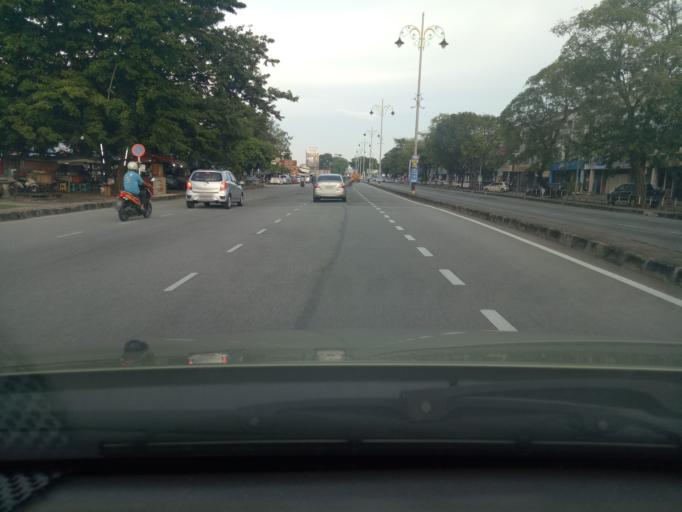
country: MY
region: Kedah
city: Alor Setar
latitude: 6.1262
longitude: 100.3550
